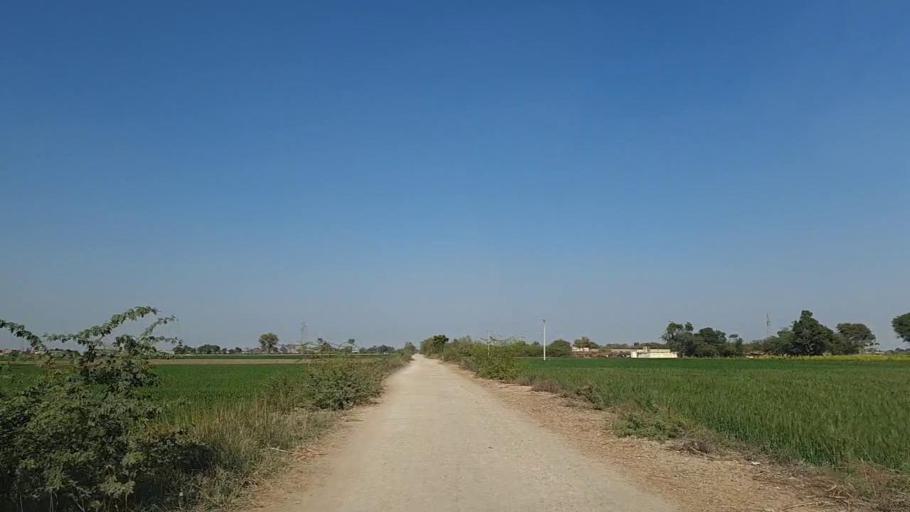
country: PK
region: Sindh
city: Nawabshah
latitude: 26.2476
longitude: 68.4410
